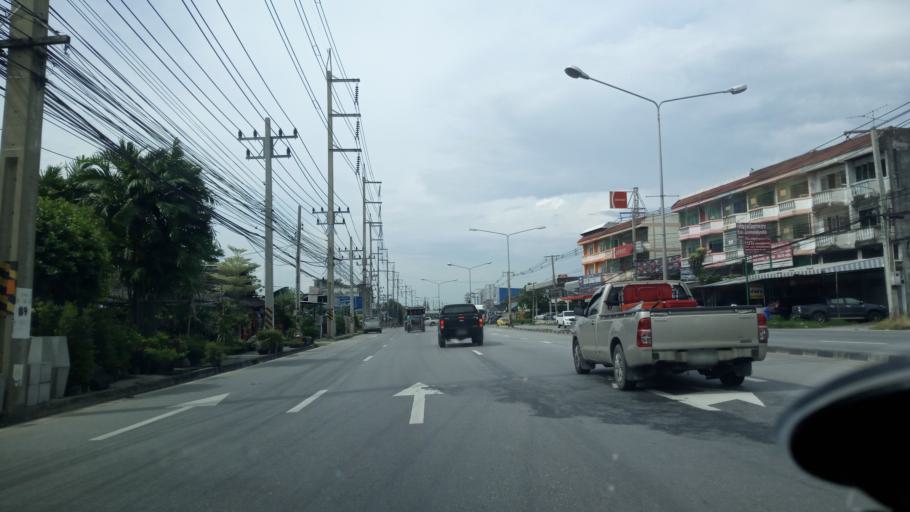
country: TH
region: Chon Buri
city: Chon Buri
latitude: 13.3934
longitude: 101.0219
